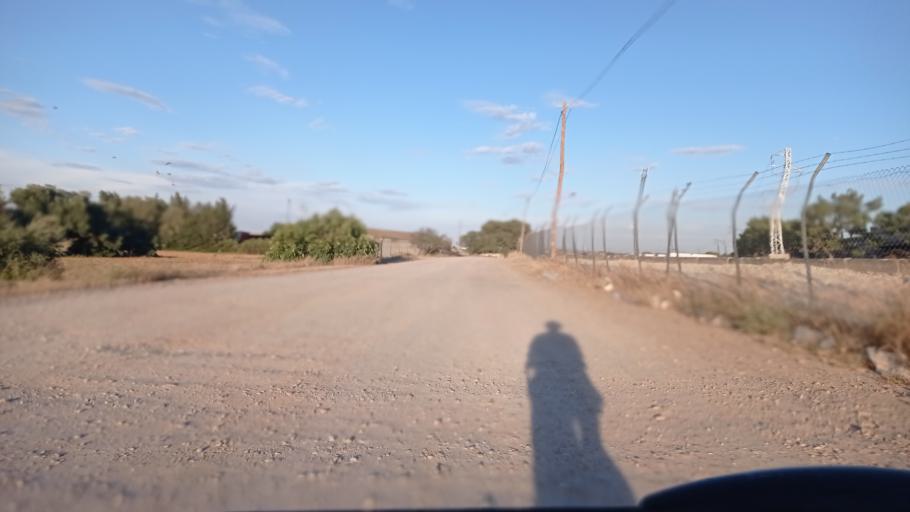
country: ES
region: Aragon
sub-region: Provincia de Zaragoza
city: Oliver-Valdefierro, Oliver, Valdefierro
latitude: 41.6762
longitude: -0.9486
